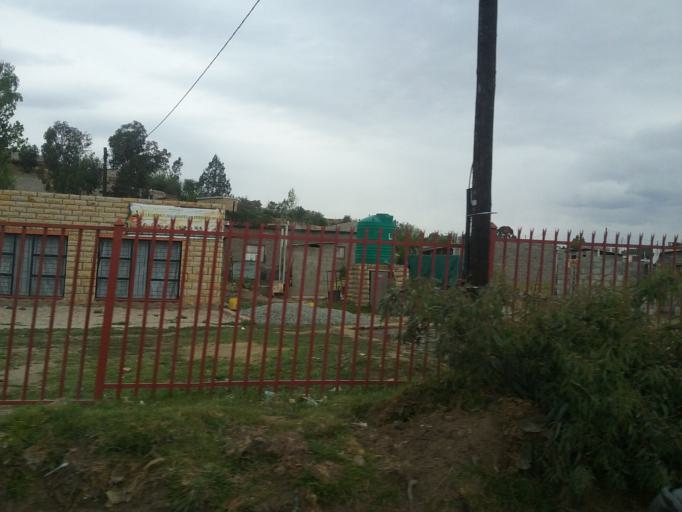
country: LS
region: Maseru
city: Maseru
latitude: -29.3293
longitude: 27.5070
